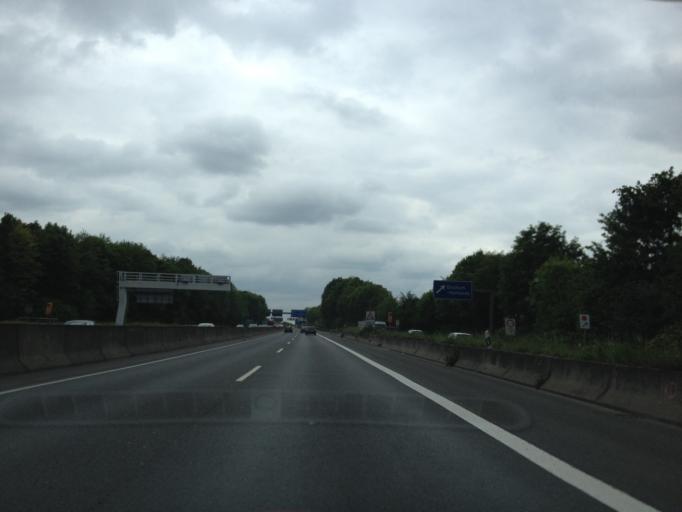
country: DE
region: North Rhine-Westphalia
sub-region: Regierungsbezirk Arnsberg
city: Bochum
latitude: 51.4980
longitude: 7.2092
